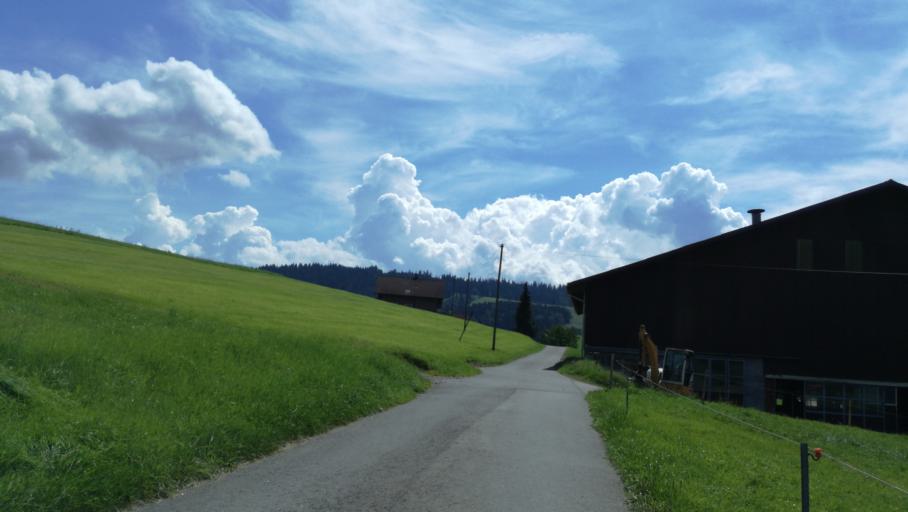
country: CH
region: Schwyz
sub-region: Bezirk Schwyz
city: Rothenthurm
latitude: 47.1393
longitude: 8.6386
